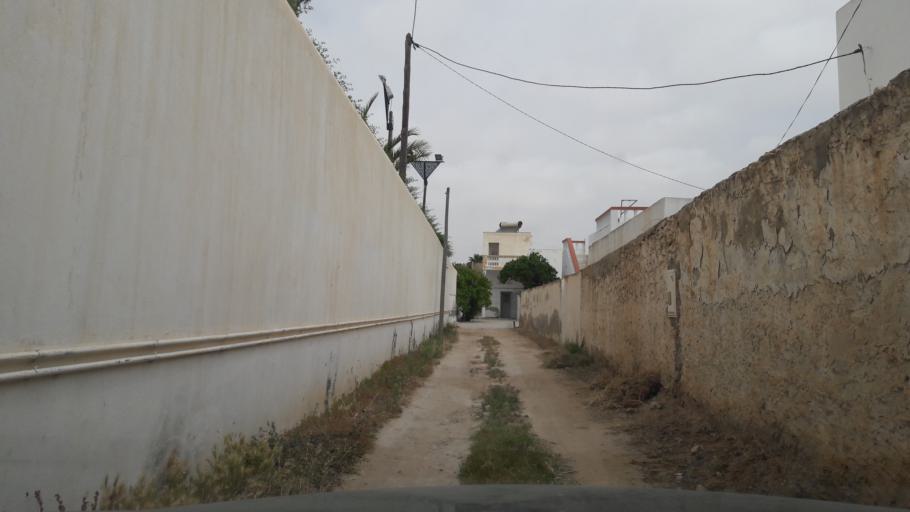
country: TN
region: Safaqis
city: Sfax
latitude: 34.7733
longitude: 10.7556
